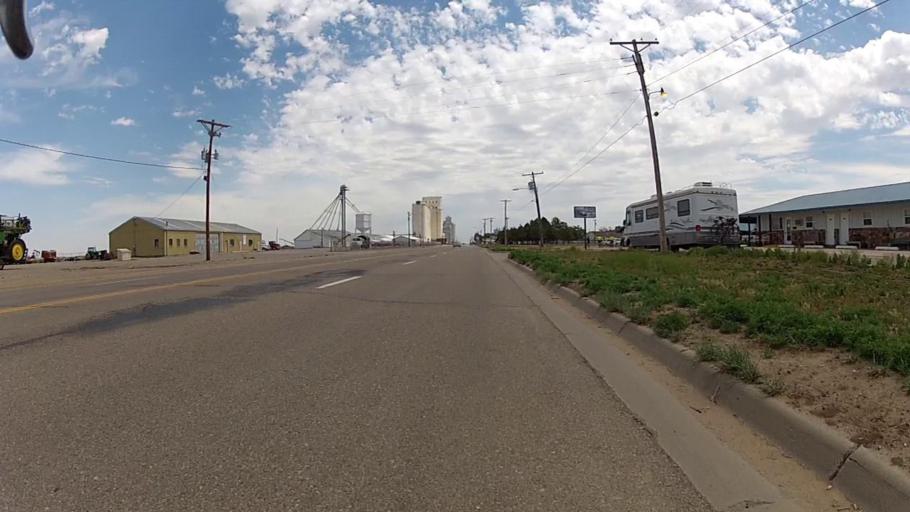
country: US
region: Kansas
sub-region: Haskell County
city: Satanta
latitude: 37.4372
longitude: -100.9956
